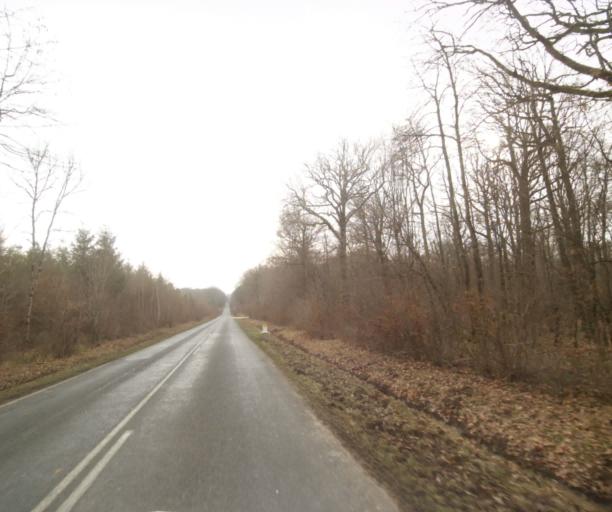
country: FR
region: Champagne-Ardenne
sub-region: Departement de la Haute-Marne
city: Villiers-en-Lieu
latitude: 48.7161
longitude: 4.8817
